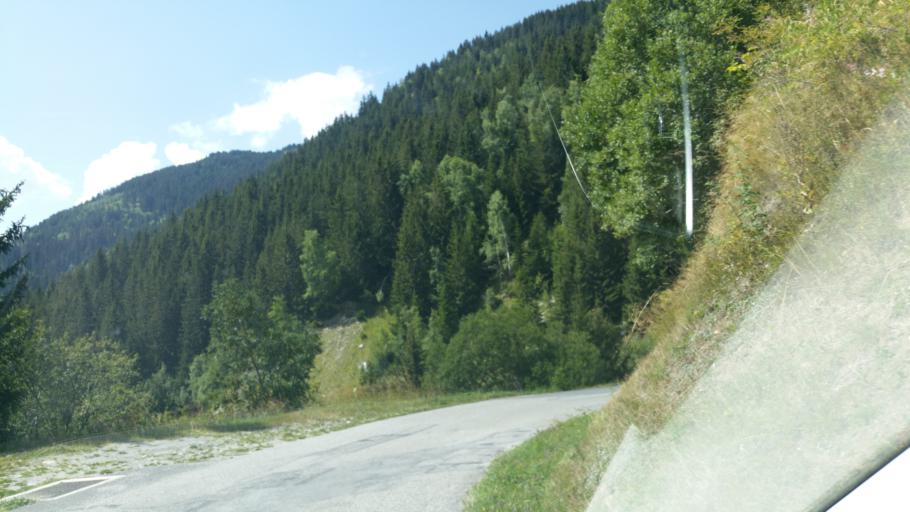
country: FR
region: Rhone-Alpes
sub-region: Departement de la Savoie
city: La Chambre
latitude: 45.4158
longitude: 6.3447
